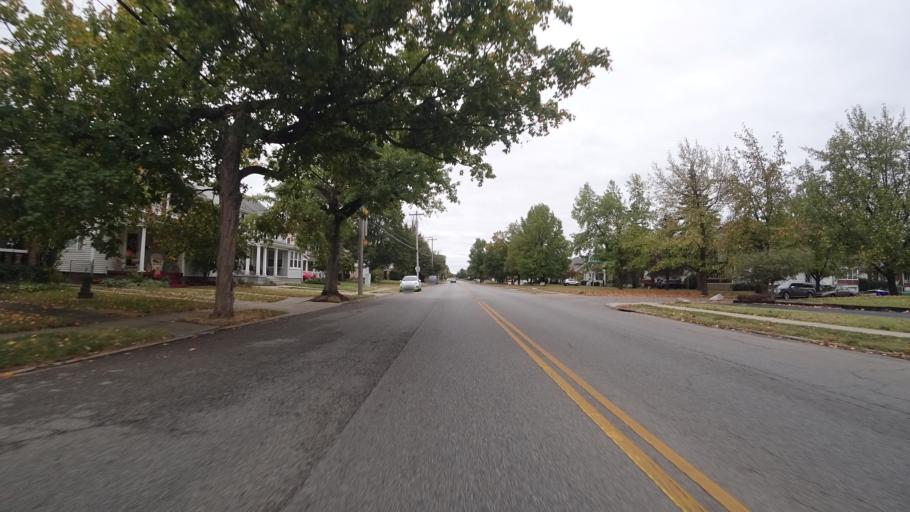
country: US
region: Ohio
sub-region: Butler County
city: Fairfield
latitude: 39.3662
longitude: -84.5577
